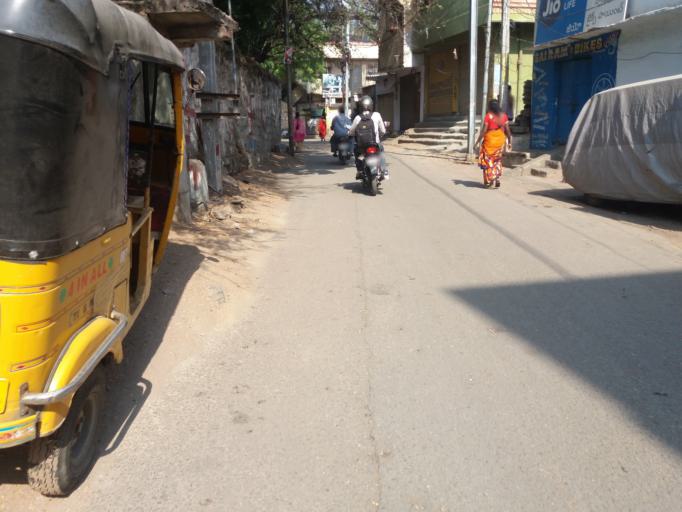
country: IN
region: Telangana
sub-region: Hyderabad
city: Malkajgiri
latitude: 17.4155
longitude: 78.5106
